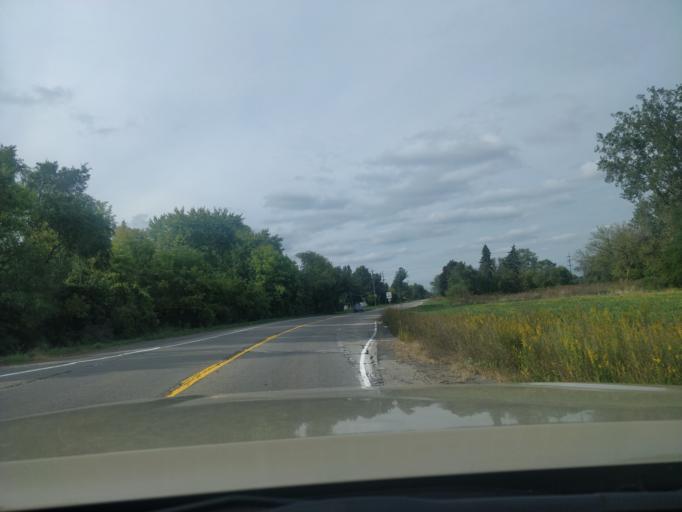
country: US
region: Michigan
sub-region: Wayne County
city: Belleville
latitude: 42.2258
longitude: -83.4447
